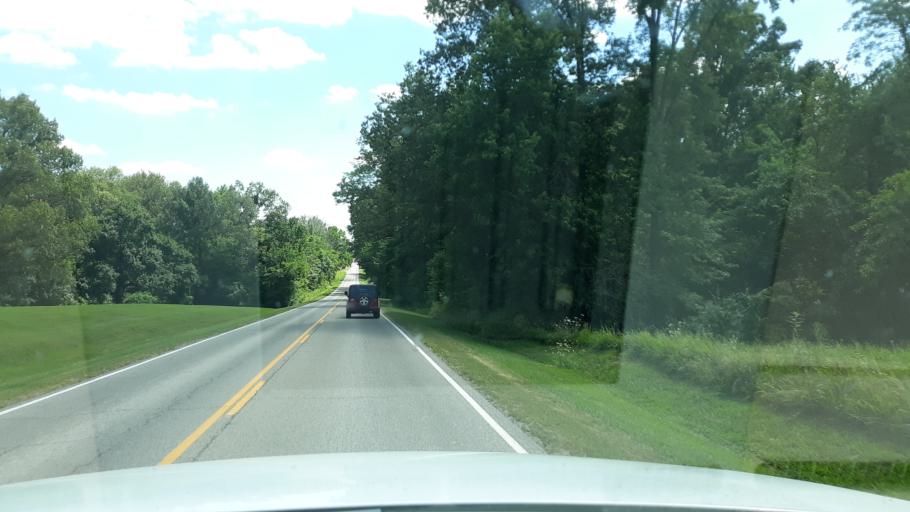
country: US
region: Illinois
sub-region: Saline County
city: Harrisburg
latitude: 37.8511
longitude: -88.6055
